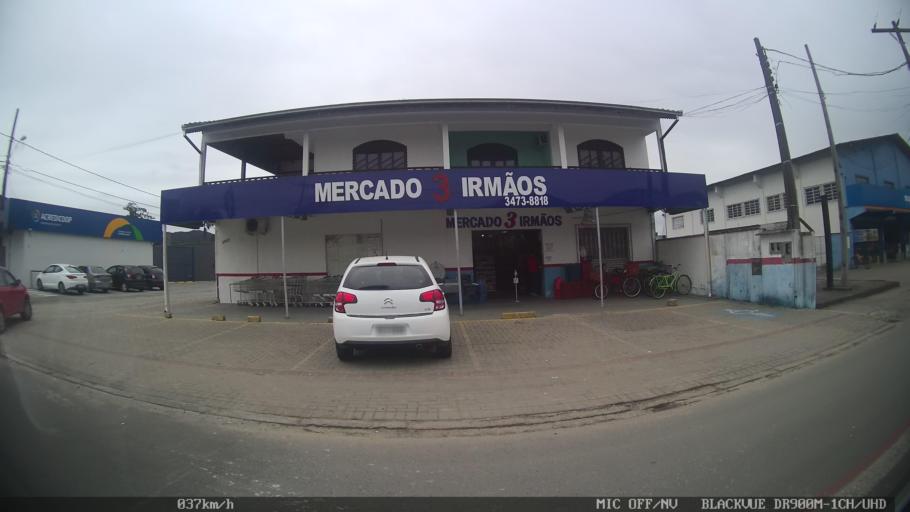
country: BR
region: Santa Catarina
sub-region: Joinville
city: Joinville
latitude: -26.2703
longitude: -48.8148
